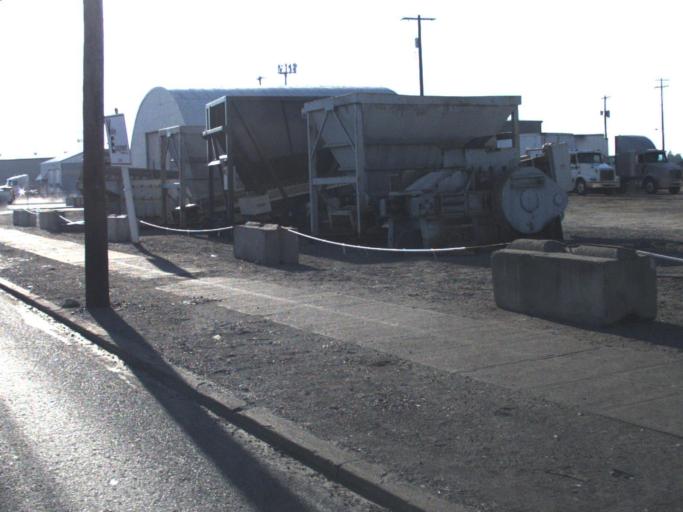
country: US
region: Washington
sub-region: Spokane County
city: Millwood
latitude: 47.6702
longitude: -117.3550
